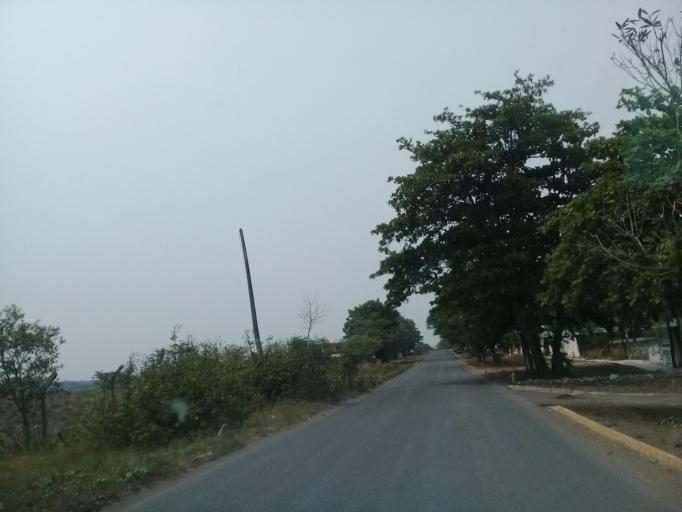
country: MX
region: Veracruz
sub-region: Medellin
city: La Laguna y Monte del Castillo
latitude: 18.9740
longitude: -96.1196
